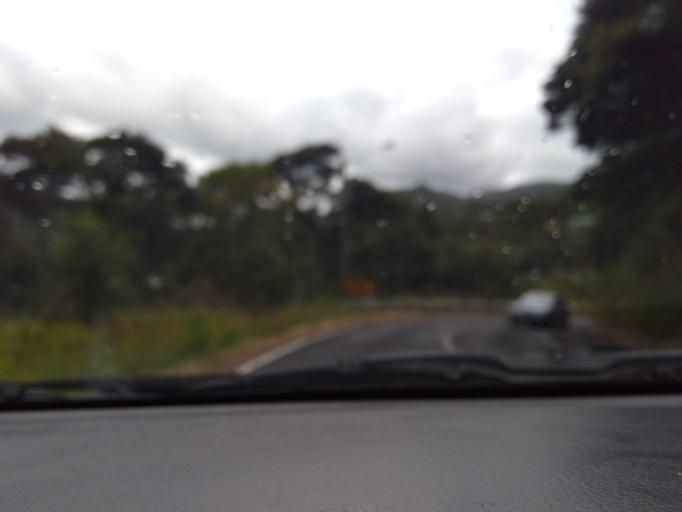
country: NZ
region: Auckland
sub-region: Auckland
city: Titirangi
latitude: -37.0026
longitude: 174.5721
